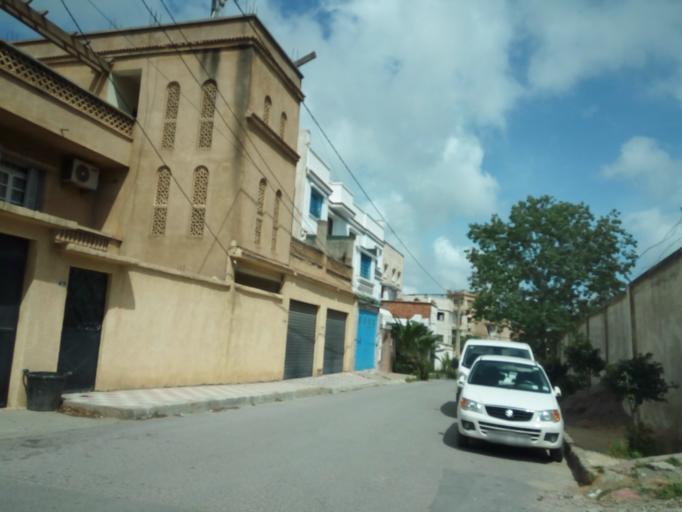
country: DZ
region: Tipaza
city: Douera
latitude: 36.7009
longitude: 2.9705
